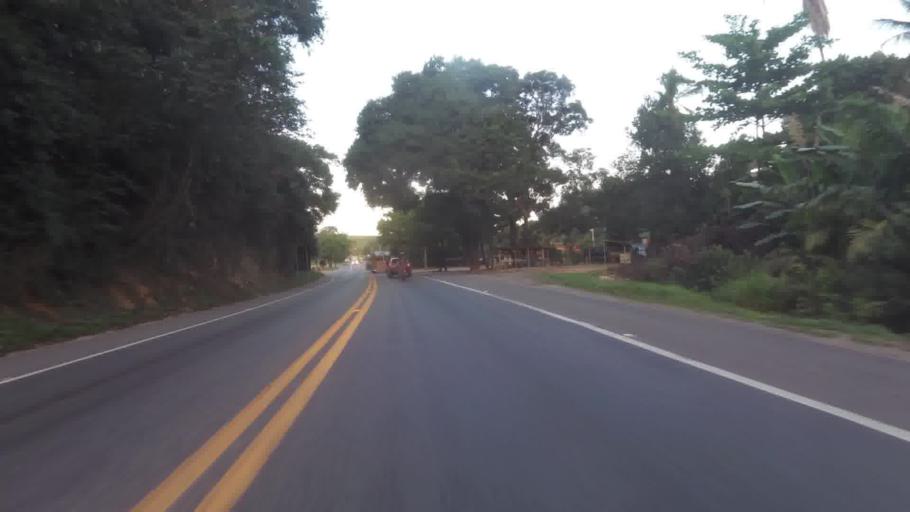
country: BR
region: Espirito Santo
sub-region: Iconha
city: Iconha
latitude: -20.7708
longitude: -40.7664
